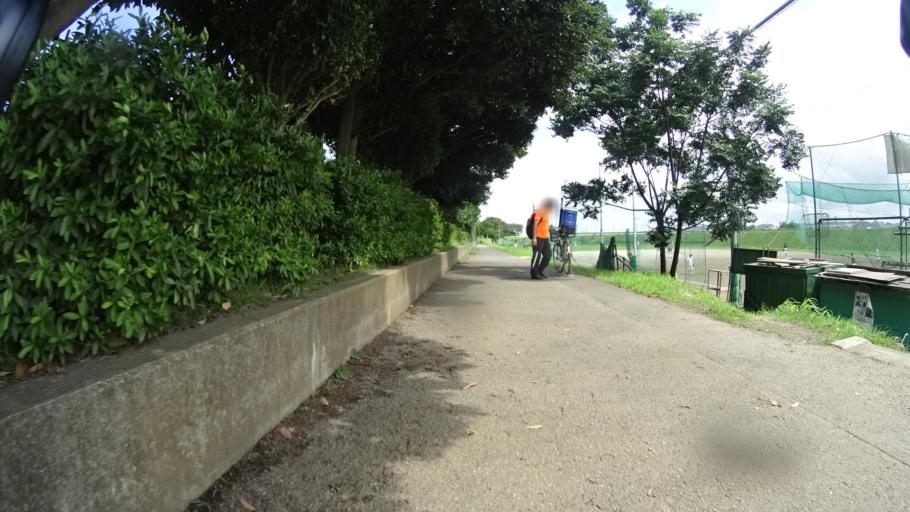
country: JP
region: Tokyo
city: Hino
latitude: 35.6858
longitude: 139.4112
